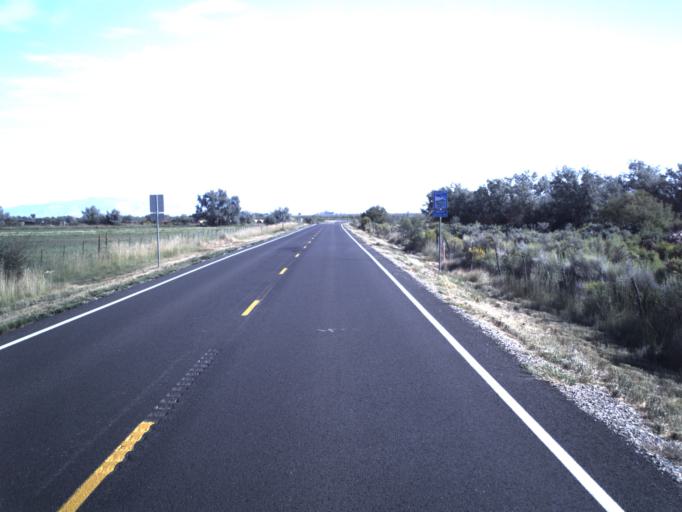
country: US
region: Utah
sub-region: Sevier County
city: Salina
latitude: 39.0133
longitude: -111.8538
